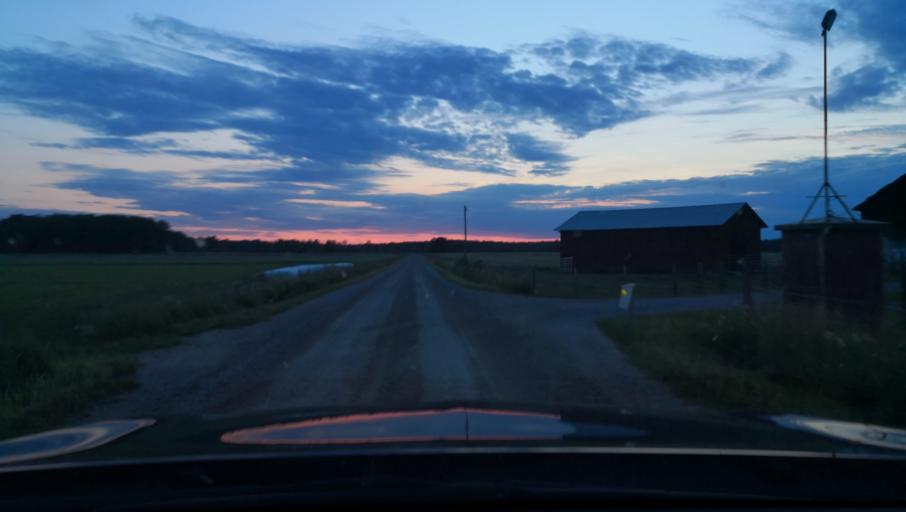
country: SE
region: Uppsala
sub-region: Osthammars Kommun
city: Bjorklinge
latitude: 60.0080
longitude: 17.3297
